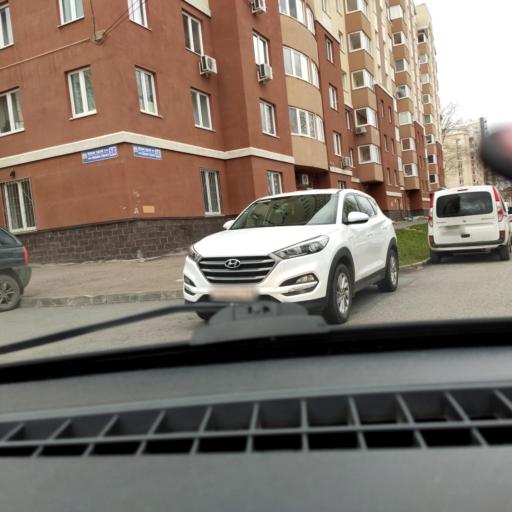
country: RU
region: Bashkortostan
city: Ufa
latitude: 54.8253
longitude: 56.0757
